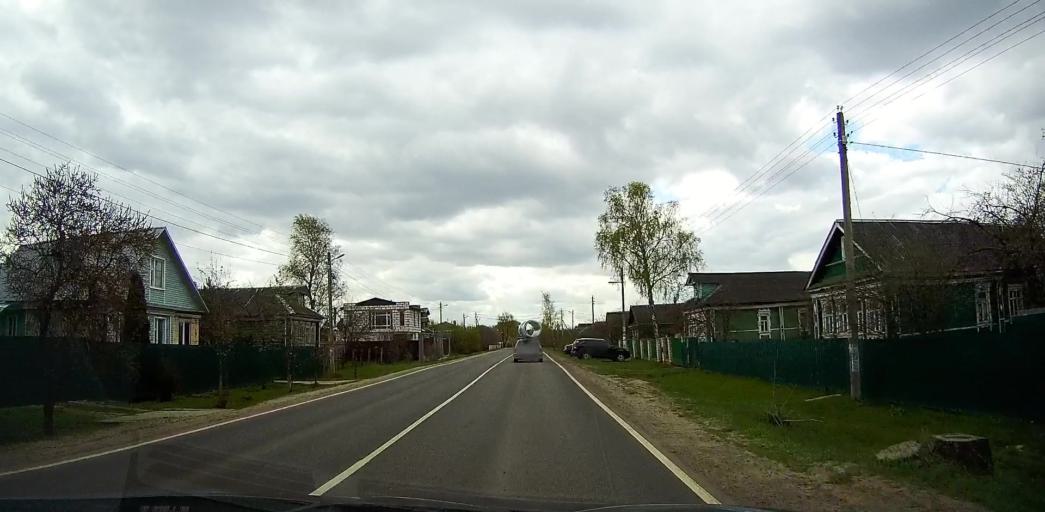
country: RU
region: Moskovskaya
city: Beloozerskiy
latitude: 55.5113
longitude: 38.4317
